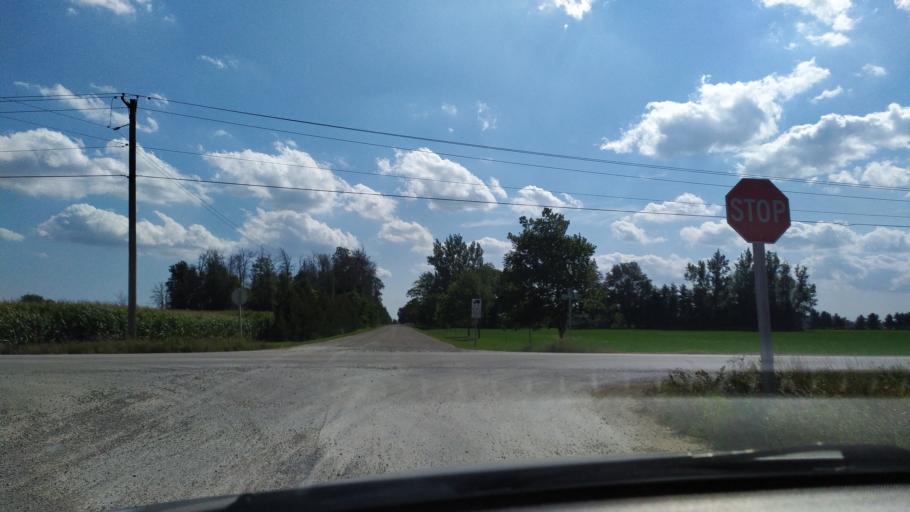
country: CA
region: Ontario
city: Stratford
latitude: 43.2641
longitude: -80.9183
